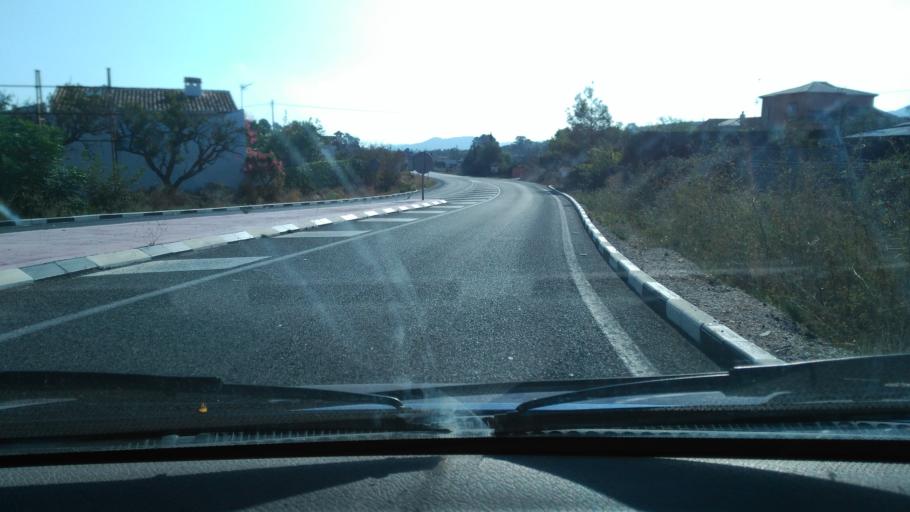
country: ES
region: Valencia
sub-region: Provincia de Alicante
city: Gata de Gorgos
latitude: 38.7845
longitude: 0.0851
